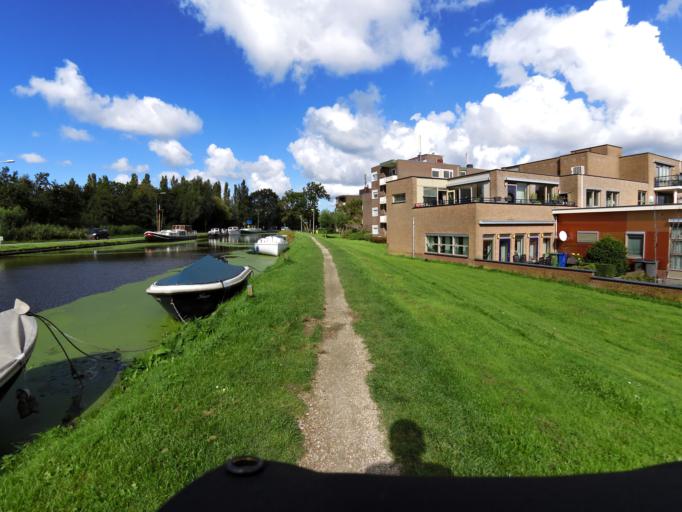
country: NL
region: South Holland
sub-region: Gemeente Delft
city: Delft
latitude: 51.9741
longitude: 4.3110
